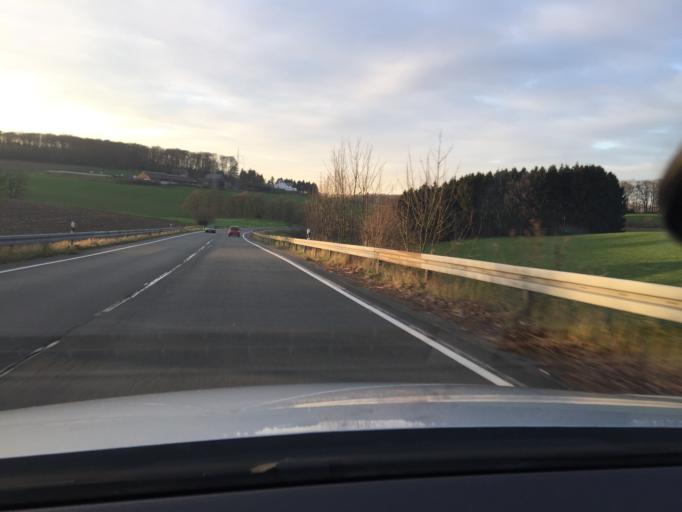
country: DE
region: North Rhine-Westphalia
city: Sprockhovel
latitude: 51.3428
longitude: 7.2121
